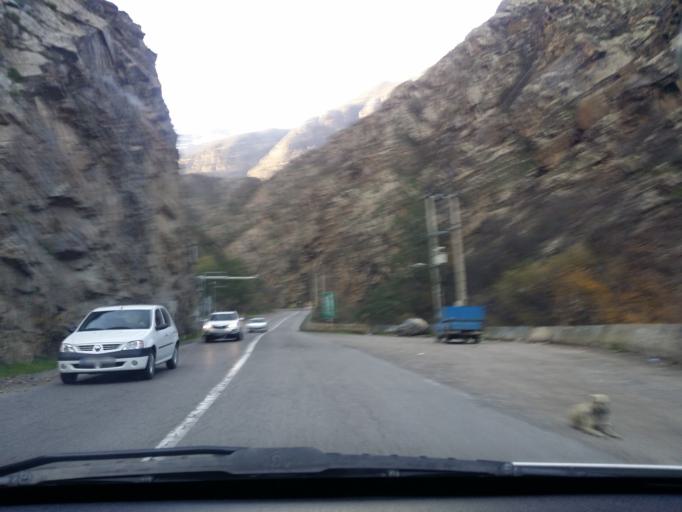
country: IR
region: Mazandaran
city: Chalus
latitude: 36.3005
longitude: 51.2484
